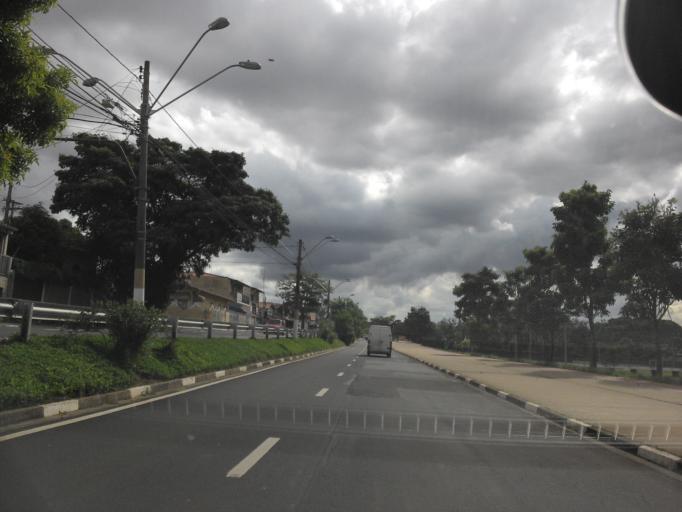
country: BR
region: Sao Paulo
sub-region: Campinas
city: Campinas
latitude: -22.8744
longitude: -47.0418
